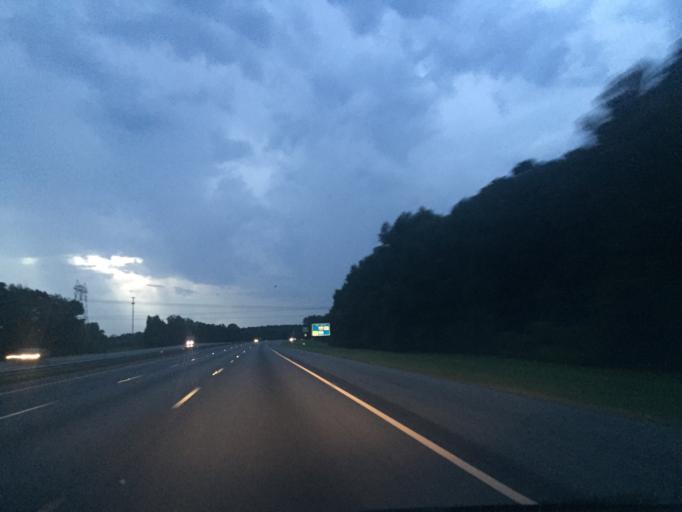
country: US
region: Georgia
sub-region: Bryan County
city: Richmond Hill
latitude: 31.9402
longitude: -81.3349
